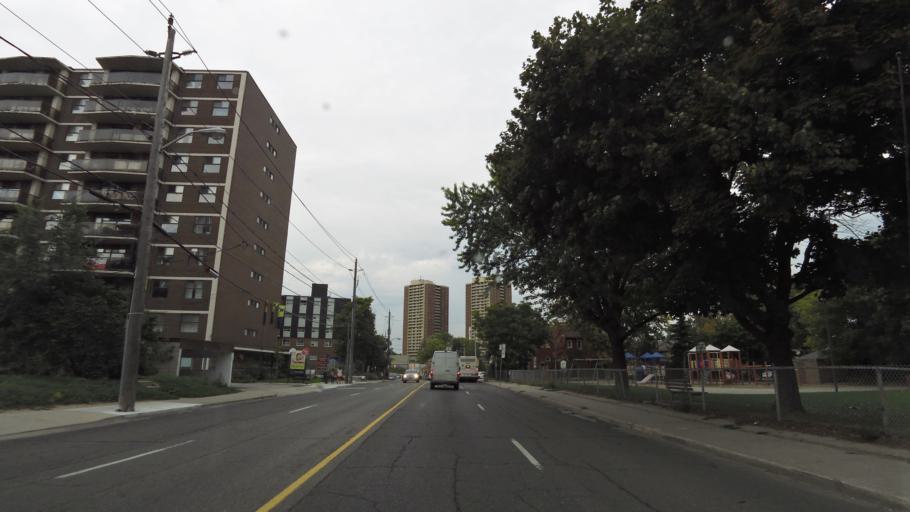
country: CA
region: Ontario
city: Etobicoke
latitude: 43.7056
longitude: -79.5302
